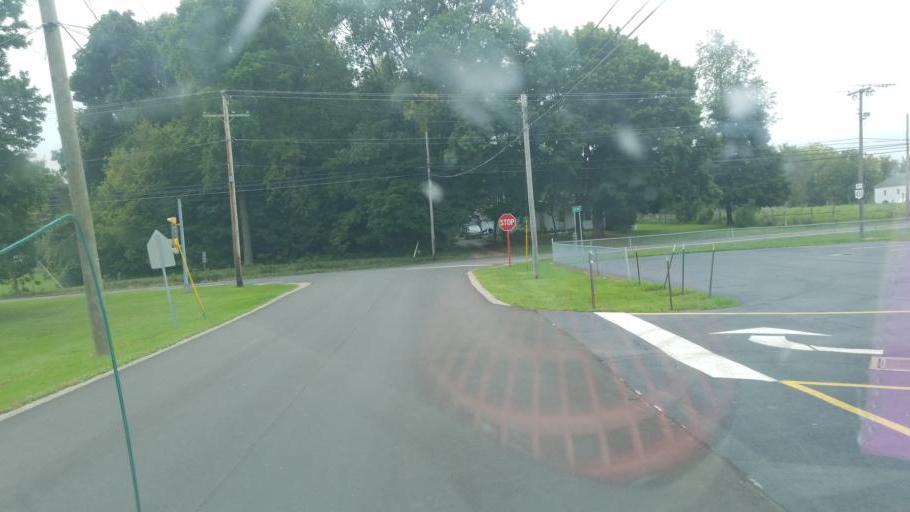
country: US
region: Ohio
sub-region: Richland County
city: Lincoln Heights
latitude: 40.7668
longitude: -82.4272
